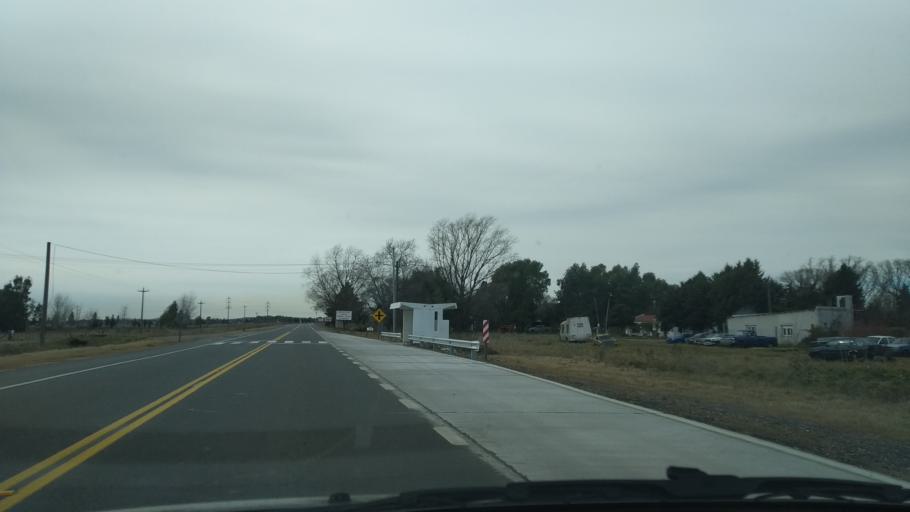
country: AR
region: Buenos Aires
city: Olavarria
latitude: -36.9899
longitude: -60.3120
